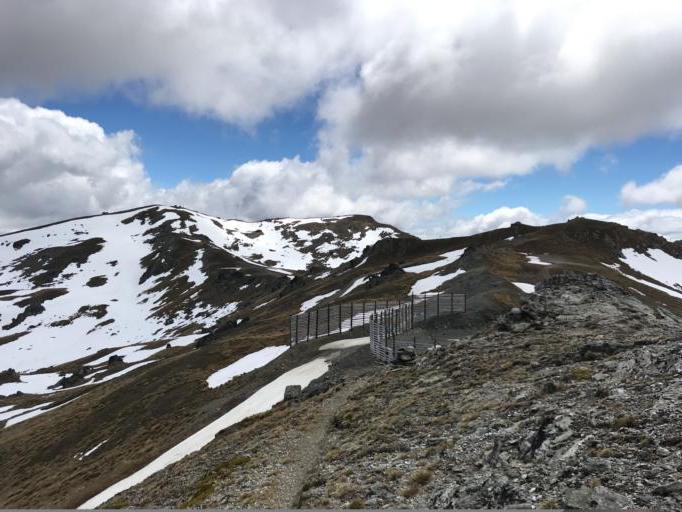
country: NZ
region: Otago
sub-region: Queenstown-Lakes District
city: Arrowtown
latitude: -44.8595
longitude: 168.9447
